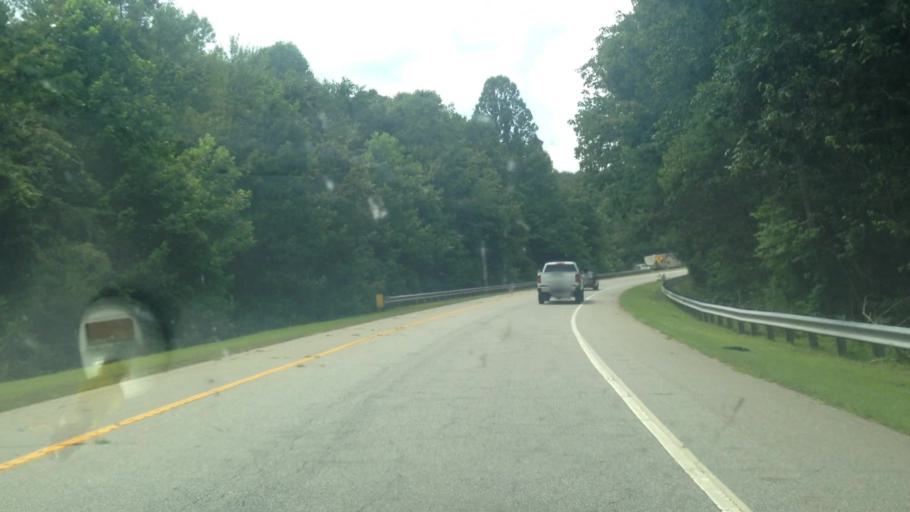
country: US
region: North Carolina
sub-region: Forsyth County
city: Rural Hall
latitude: 36.2034
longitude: -80.2941
